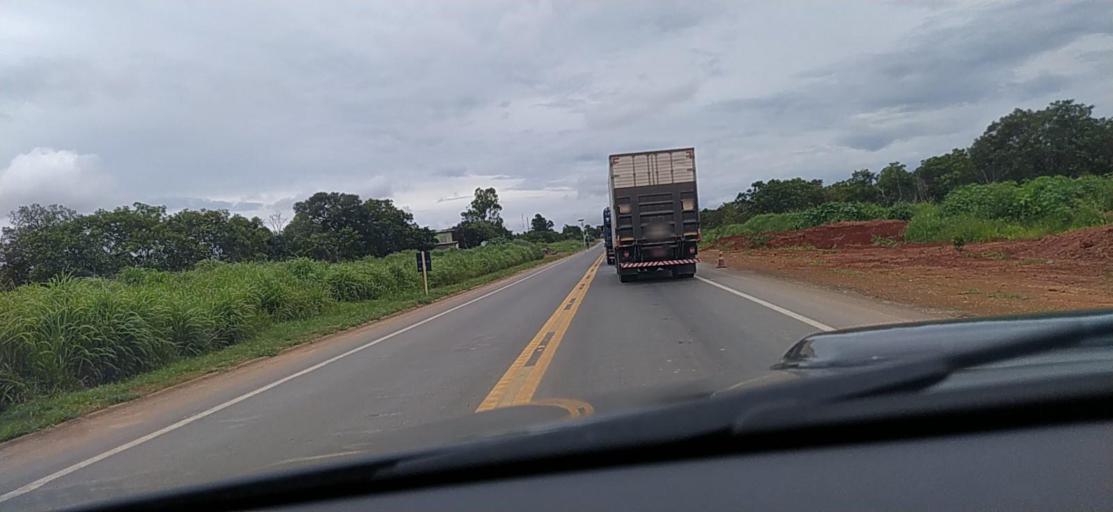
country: BR
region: Minas Gerais
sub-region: Curvelo
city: Curvelo
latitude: -18.7177
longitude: -44.4423
